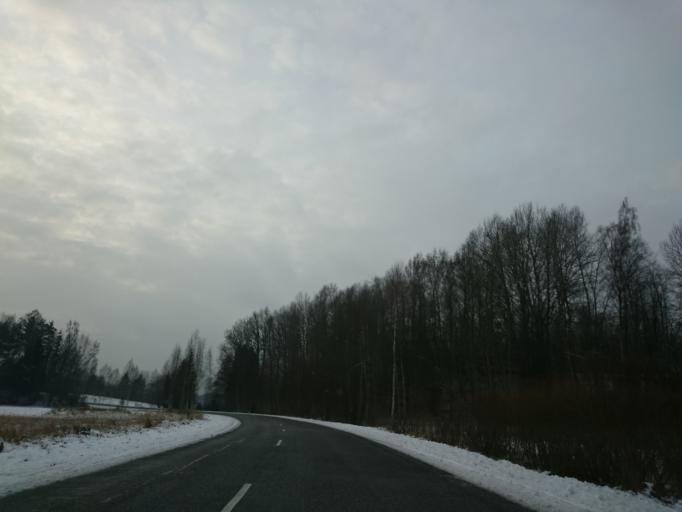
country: LV
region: Seja
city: Loja
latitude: 57.1920
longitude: 24.5974
